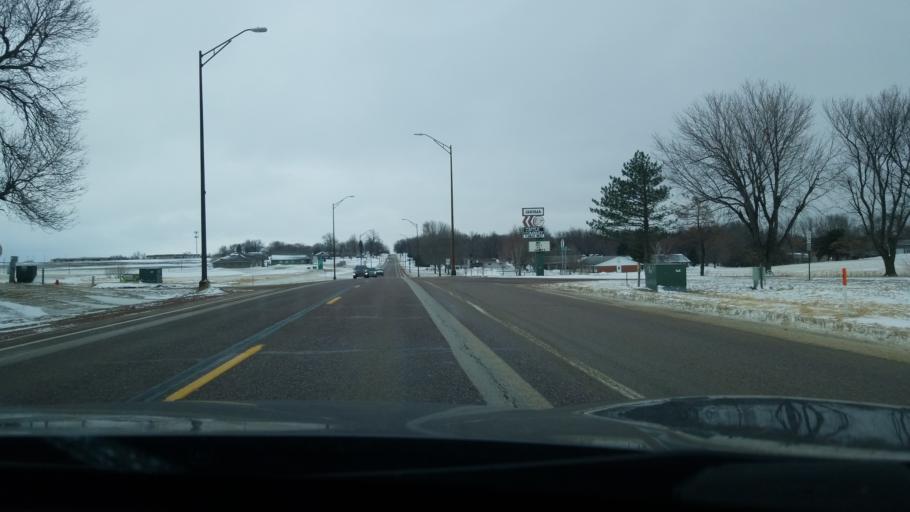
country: US
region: Iowa
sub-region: Lyon County
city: Rock Rapids
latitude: 43.4184
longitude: -96.1758
